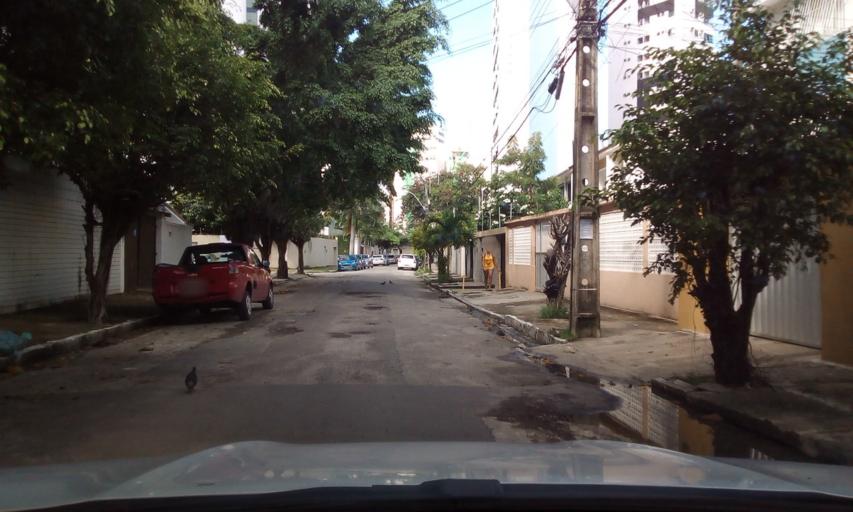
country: BR
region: Pernambuco
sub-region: Recife
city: Recife
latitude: -8.1273
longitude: -34.9049
